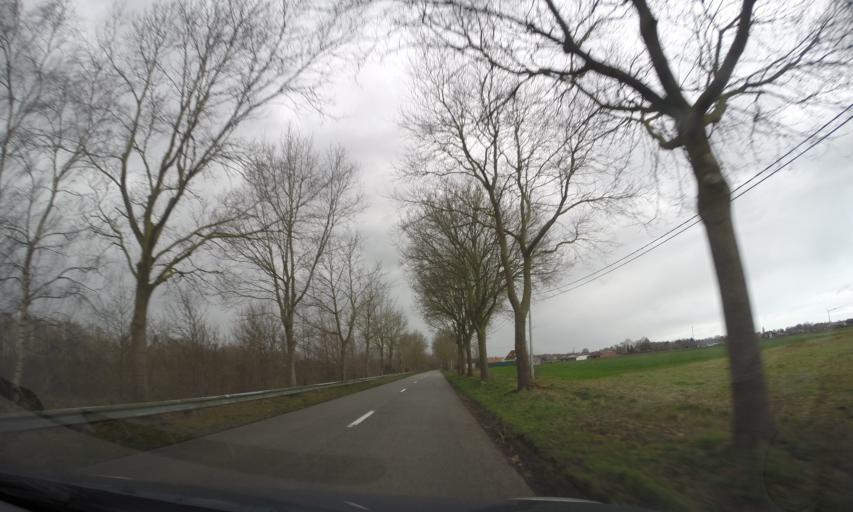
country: BE
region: Flanders
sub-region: Provincie West-Vlaanderen
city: Beernem
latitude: 51.1323
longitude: 3.3485
